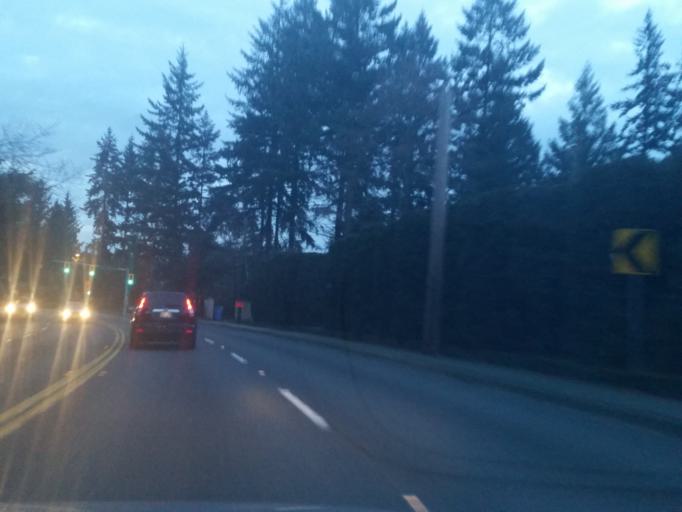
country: US
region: Washington
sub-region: Snohomish County
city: Mountlake Terrace
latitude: 47.7614
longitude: -122.3125
